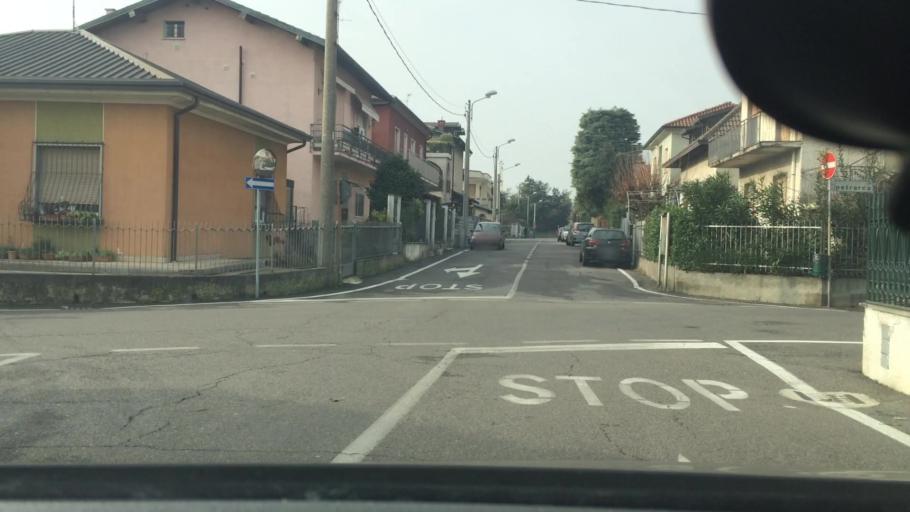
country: IT
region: Lombardy
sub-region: Provincia di Monza e Brianza
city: Villaggio del Sole
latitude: 45.6233
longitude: 9.1051
